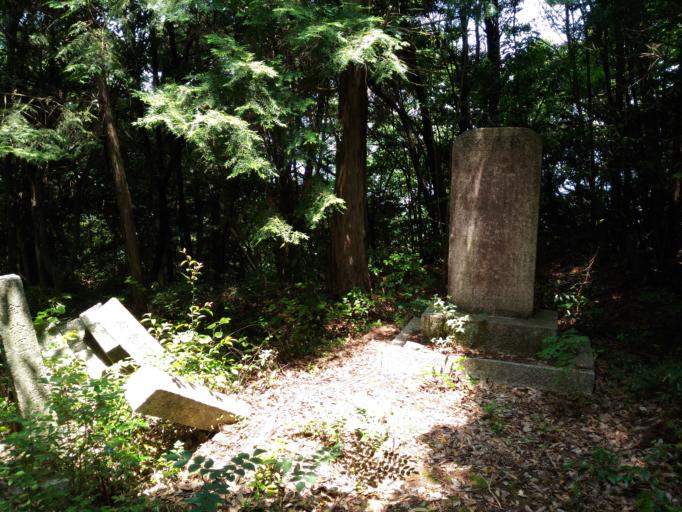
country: JP
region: Yamaguchi
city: Yamaguchi-shi
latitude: 34.1266
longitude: 131.4753
